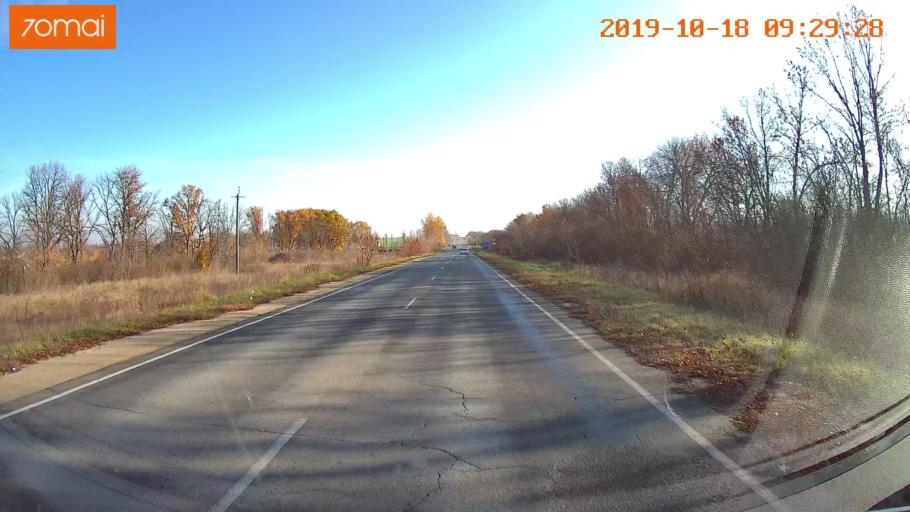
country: RU
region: Tula
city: Yefremov
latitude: 53.1378
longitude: 38.1558
